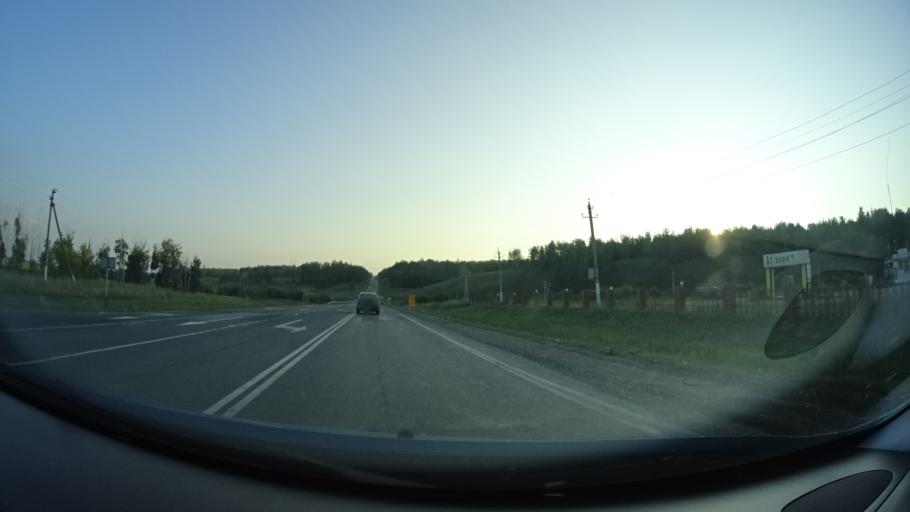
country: RU
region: Samara
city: Isakly
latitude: 54.0012
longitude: 51.5603
